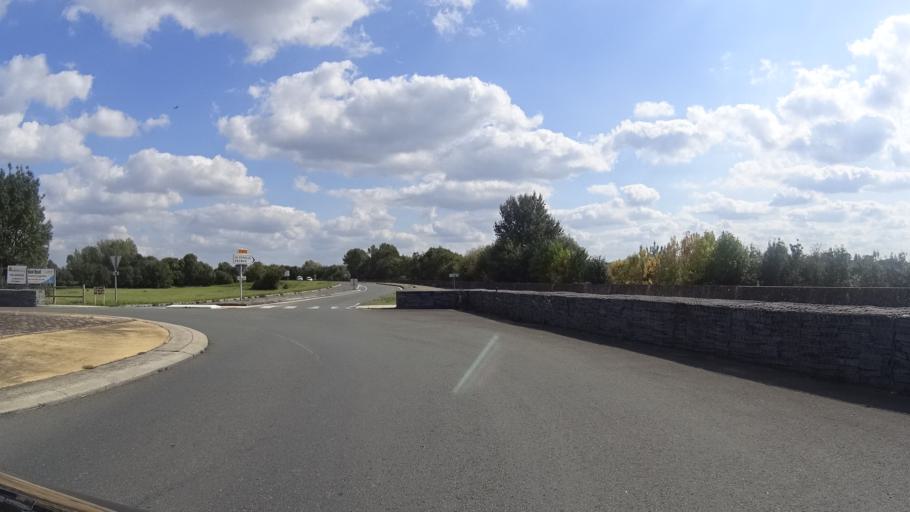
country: FR
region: Pays de la Loire
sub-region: Departement de Maine-et-Loire
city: La Dagueniere
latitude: 47.4201
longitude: -0.4492
